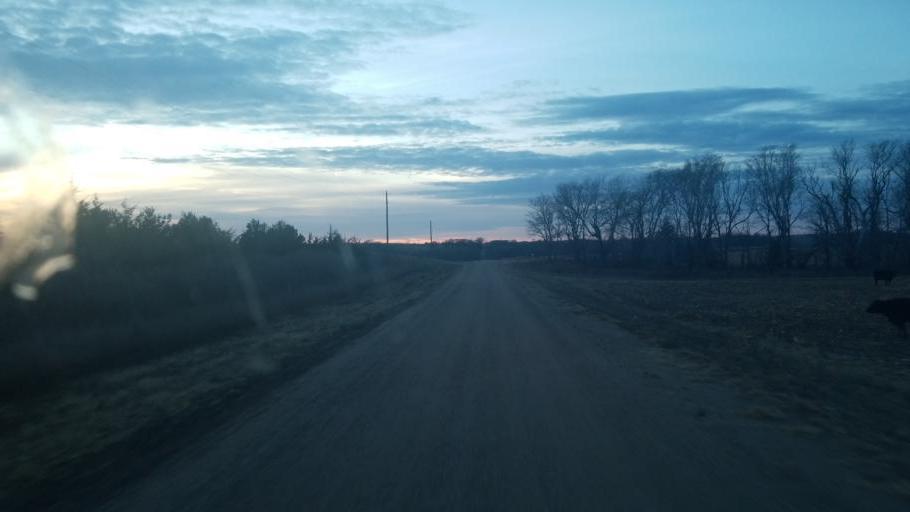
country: US
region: Nebraska
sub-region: Knox County
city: Center
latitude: 42.6554
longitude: -97.7878
